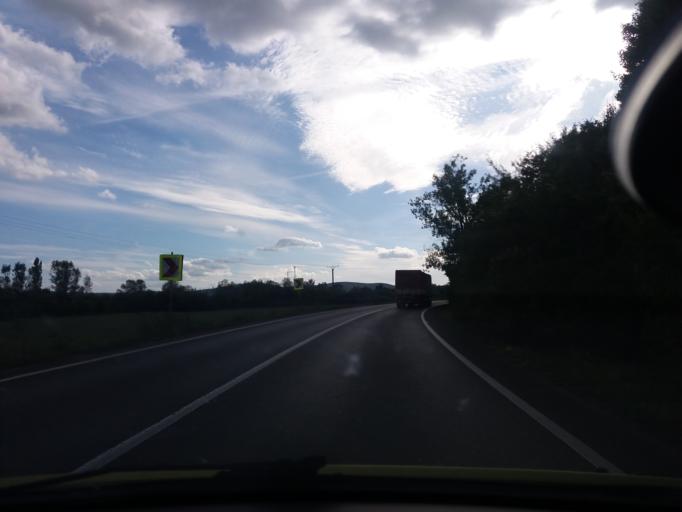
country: RO
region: Arad
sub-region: Comuna Ususau
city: Ususau
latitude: 46.0957
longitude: 21.8118
